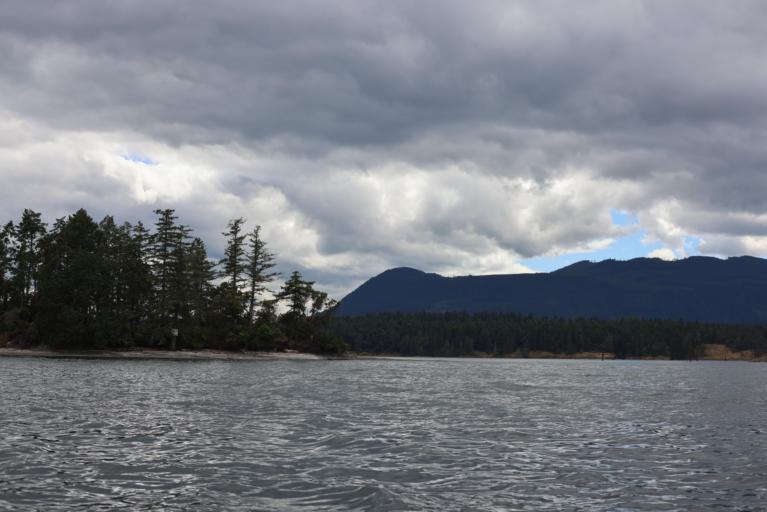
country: CA
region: British Columbia
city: North Cowichan
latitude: 48.9129
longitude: -123.6763
